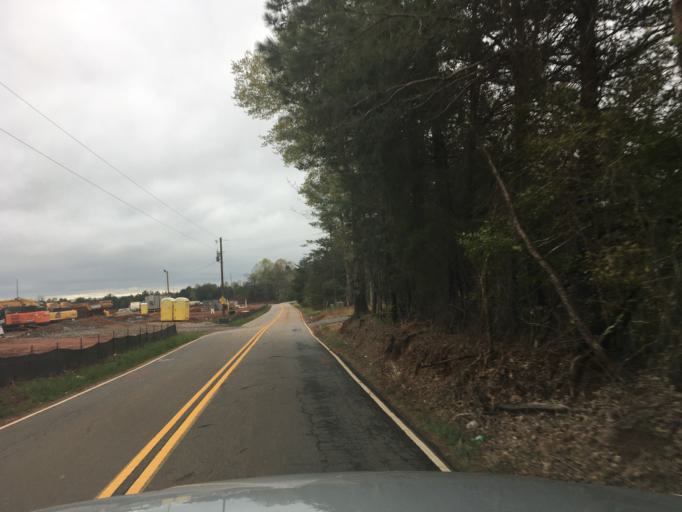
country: US
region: South Carolina
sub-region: Spartanburg County
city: Fairforest
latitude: 34.9666
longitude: -82.0503
